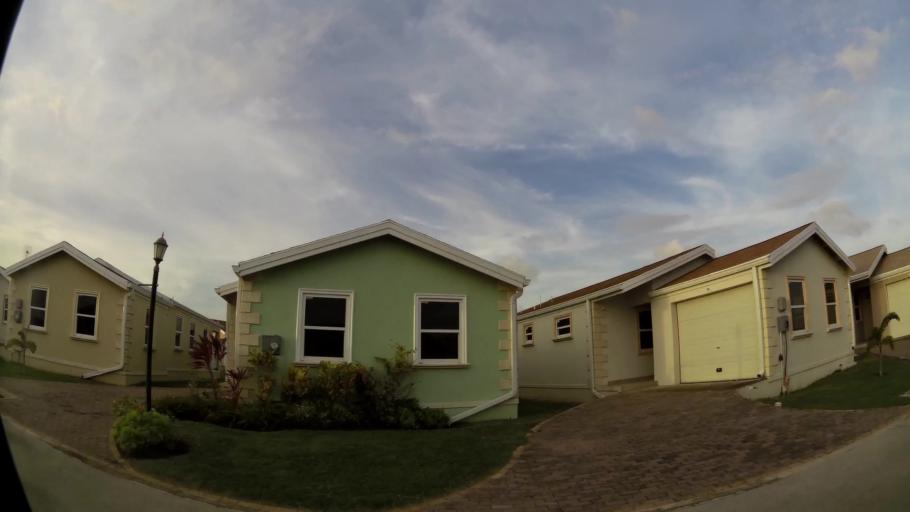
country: BB
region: Christ Church
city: Oistins
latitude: 13.0852
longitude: -59.4998
